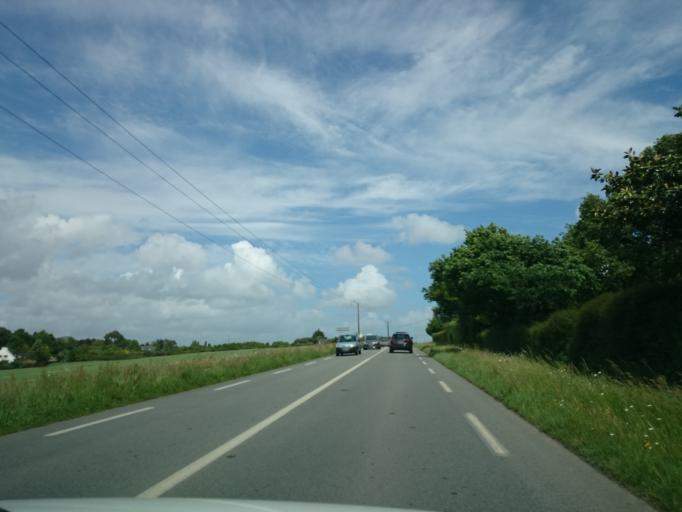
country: FR
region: Brittany
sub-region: Departement du Morbihan
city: Ploeren
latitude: 47.6222
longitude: -2.8678
